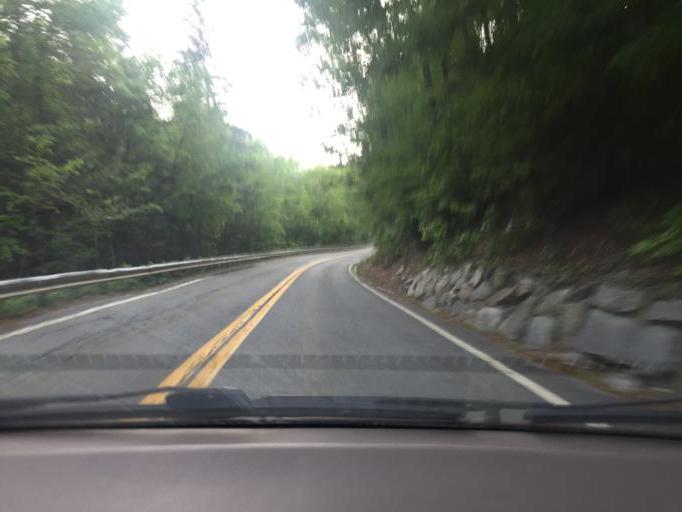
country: US
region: Massachusetts
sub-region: Middlesex County
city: Ashby
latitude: 42.6704
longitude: -71.7810
